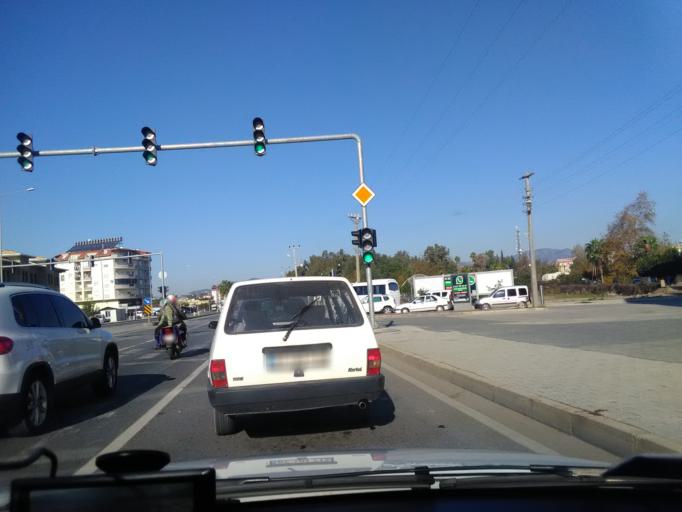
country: TR
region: Antalya
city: Gazipasa
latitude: 36.2648
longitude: 32.3185
